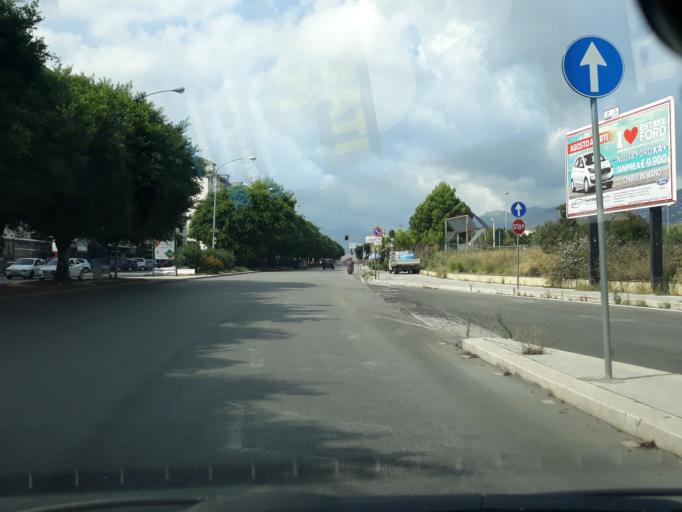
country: IT
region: Sicily
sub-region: Palermo
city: Palermo
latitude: 38.0974
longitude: 13.3453
